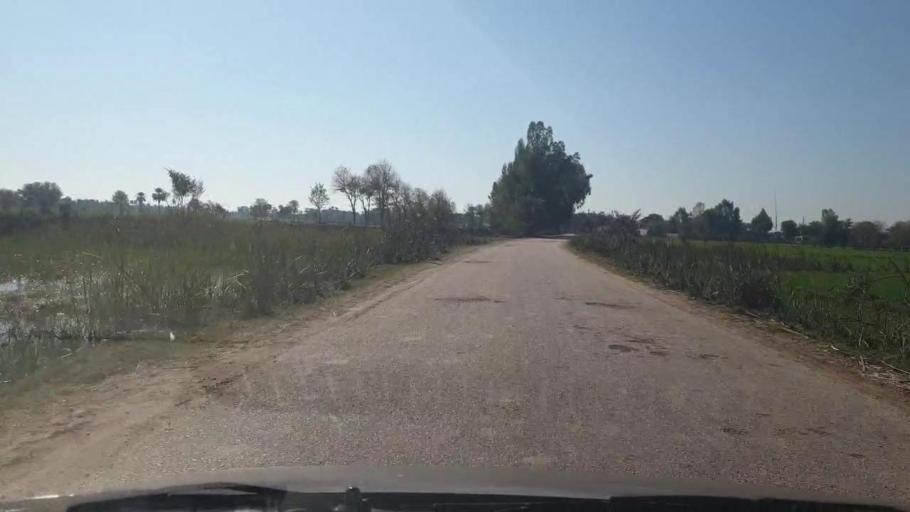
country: PK
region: Sindh
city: Bozdar
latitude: 27.0989
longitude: 68.6293
